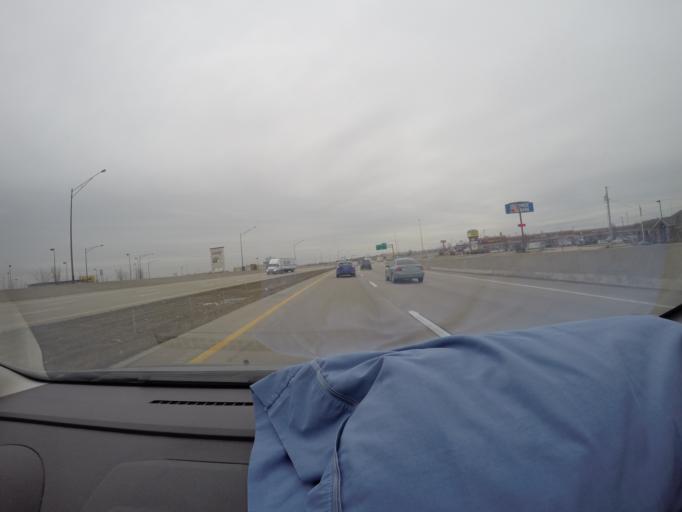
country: US
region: Missouri
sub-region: Saint Charles County
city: Wentzville
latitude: 38.8091
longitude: -90.8798
